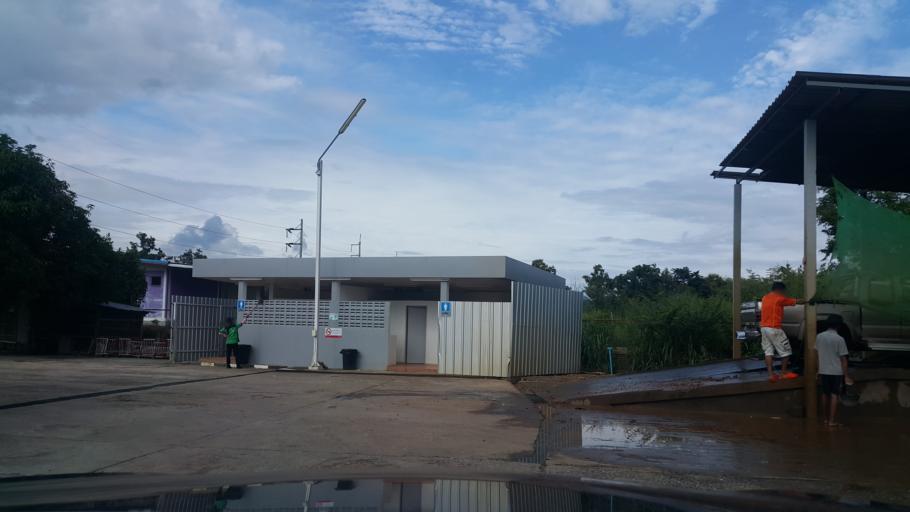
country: TH
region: Chiang Rai
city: Mae Suai
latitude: 19.6596
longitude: 99.5470
